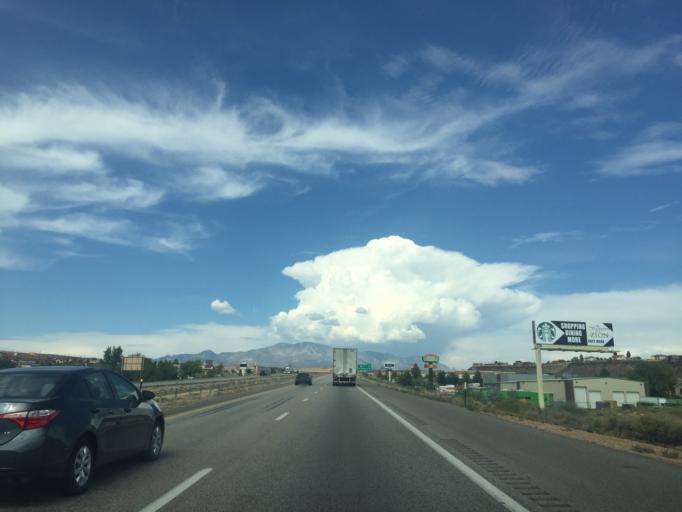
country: US
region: Utah
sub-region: Washington County
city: Saint George
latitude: 37.1026
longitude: -113.5606
